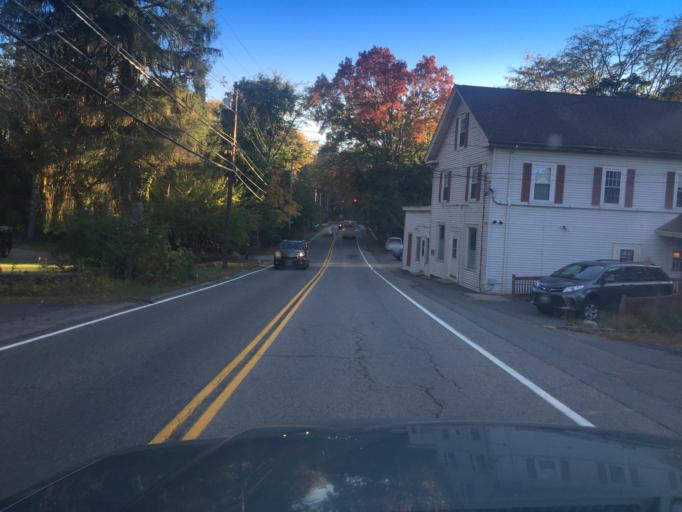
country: US
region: Massachusetts
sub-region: Middlesex County
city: Stow
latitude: 42.4064
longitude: -71.5257
